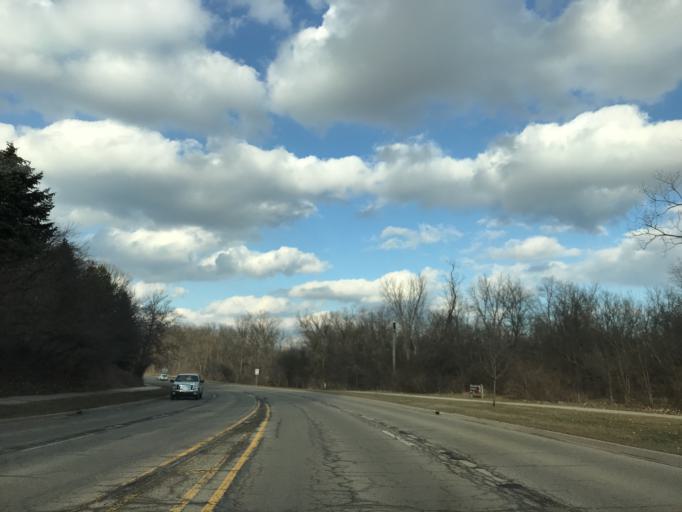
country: US
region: Michigan
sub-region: Washtenaw County
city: Ann Arbor
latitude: 42.2612
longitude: -83.6931
